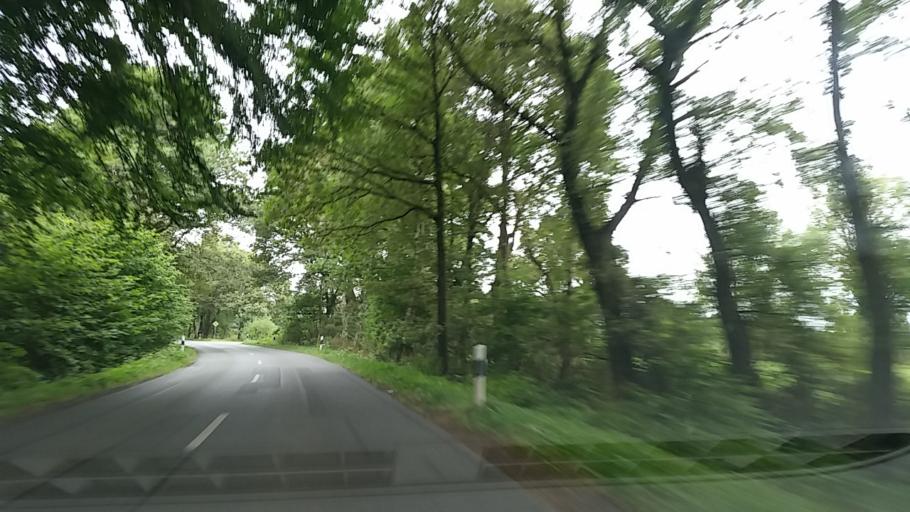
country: DE
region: Lower Saxony
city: Hipstedt
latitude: 53.4197
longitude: 8.9110
